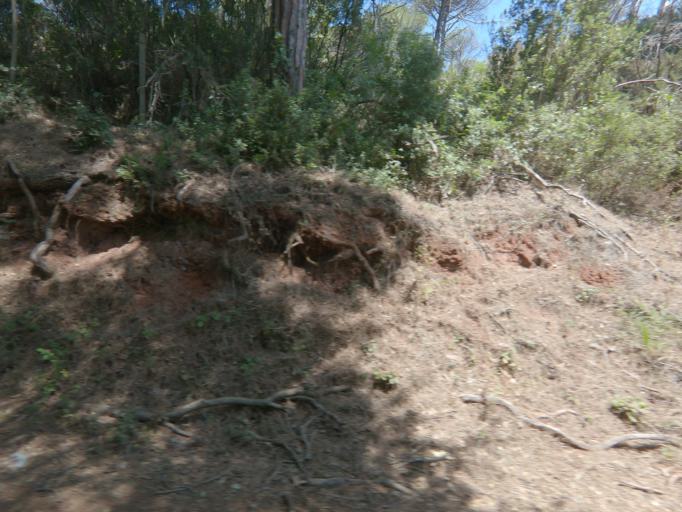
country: PT
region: Setubal
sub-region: Setubal
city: Setubal
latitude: 38.5166
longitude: -8.9308
